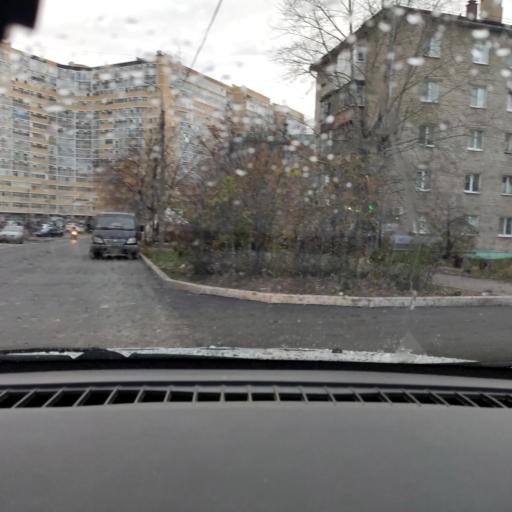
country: RU
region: Perm
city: Kondratovo
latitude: 58.0478
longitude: 56.0872
